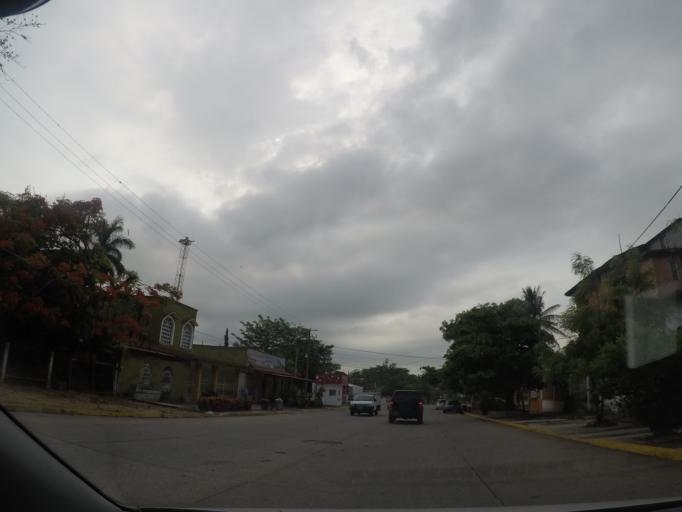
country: MX
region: Oaxaca
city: Matias Romero
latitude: 16.8744
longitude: -95.0459
